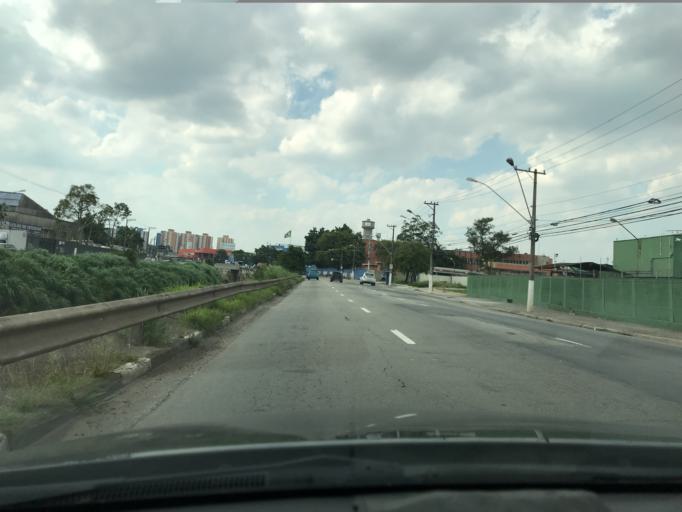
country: BR
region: Sao Paulo
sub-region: Sao Caetano Do Sul
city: Sao Caetano do Sul
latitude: -23.6132
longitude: -46.5438
